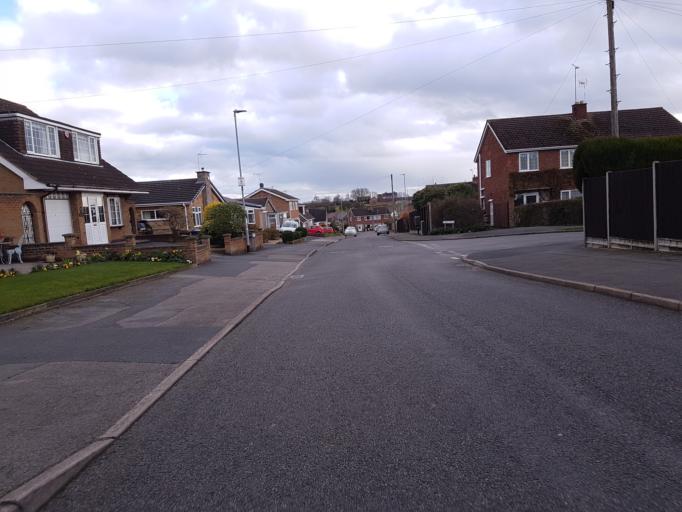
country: GB
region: England
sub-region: Leicestershire
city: Earl Shilton
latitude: 52.5691
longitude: -1.3201
